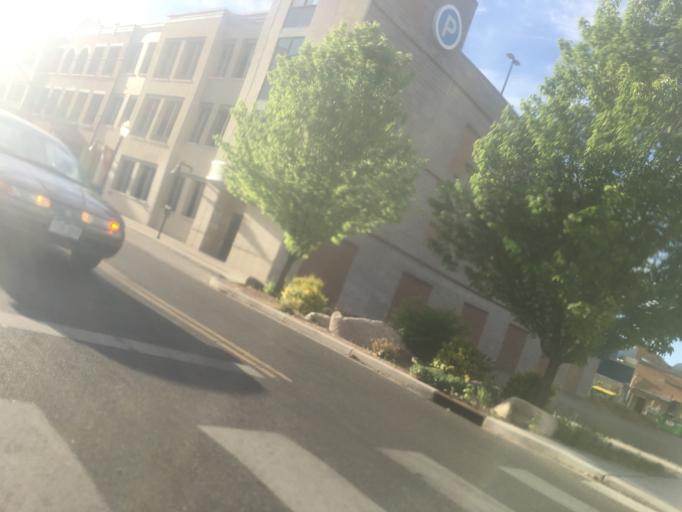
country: US
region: Colorado
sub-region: Mesa County
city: Grand Junction
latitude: 39.0683
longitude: -108.5661
